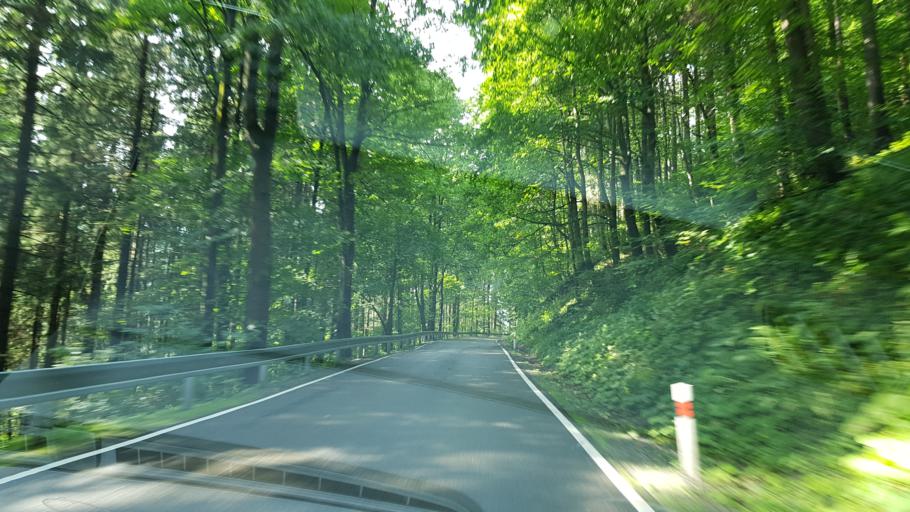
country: CZ
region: Olomoucky
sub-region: Okres Jesenik
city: Jesenik
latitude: 50.2083
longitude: 17.2448
